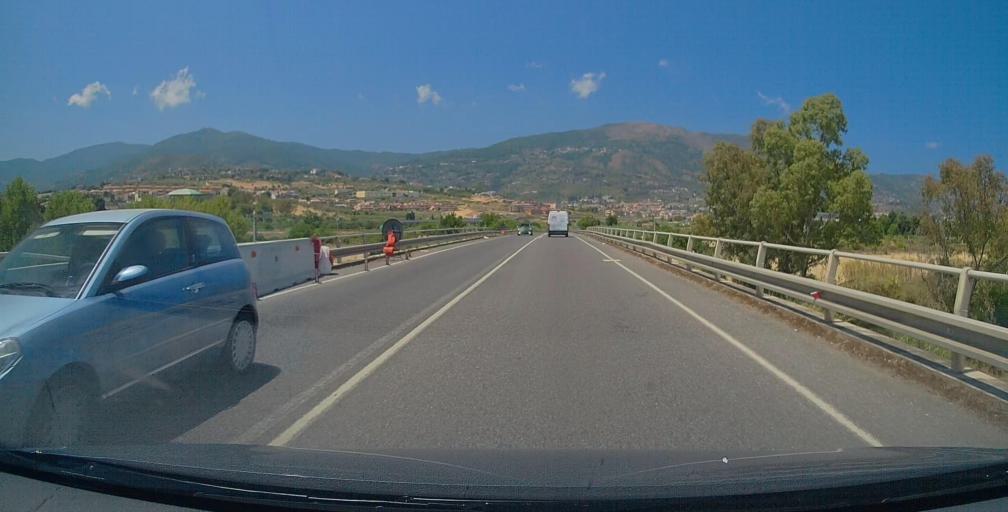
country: IT
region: Sicily
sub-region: Messina
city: Patti
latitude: 38.1456
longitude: 14.9944
